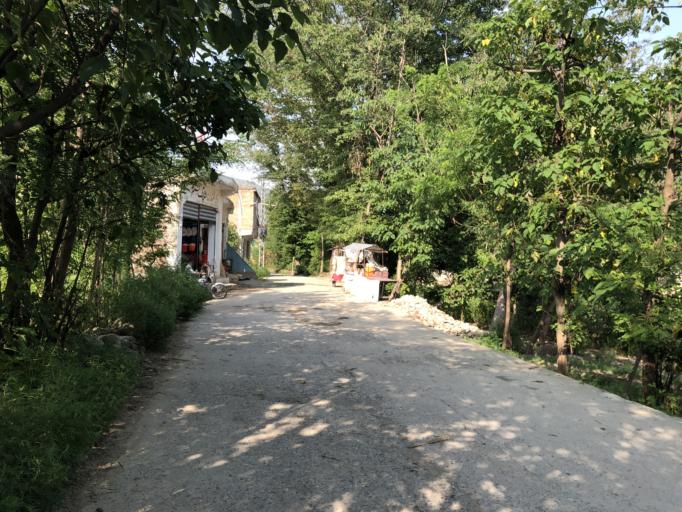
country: PK
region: Khyber Pakhtunkhwa
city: Daggar
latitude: 34.5979
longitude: 72.4512
